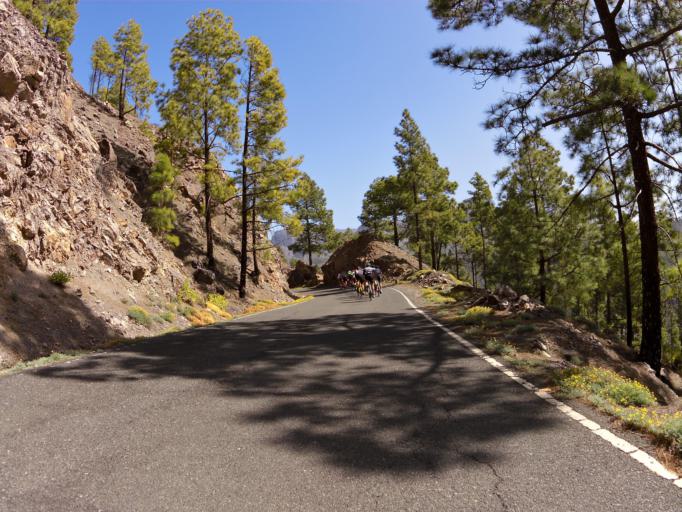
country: ES
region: Canary Islands
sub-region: Provincia de Las Palmas
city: Tejeda
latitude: 27.9379
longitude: -15.6384
